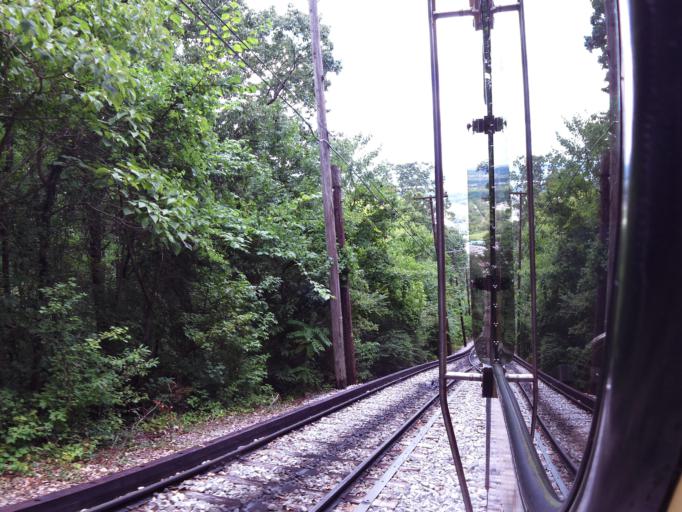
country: US
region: Tennessee
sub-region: Hamilton County
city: Lookout Mountain
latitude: 35.0079
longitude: -85.3358
